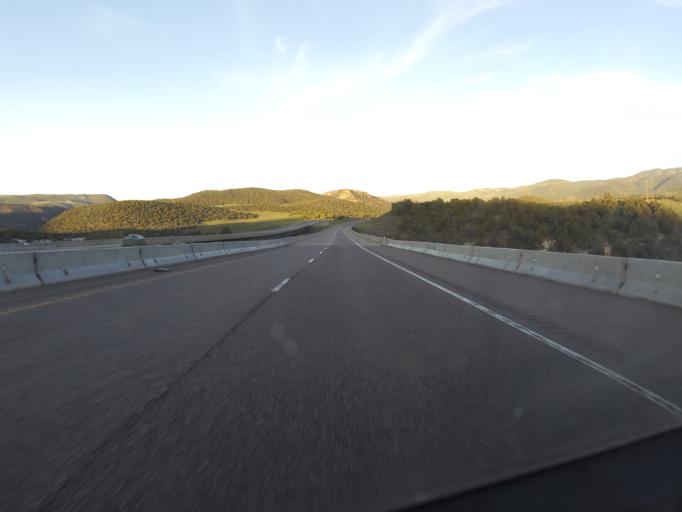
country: US
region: Utah
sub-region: Beaver County
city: Beaver
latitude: 38.5737
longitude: -112.4631
